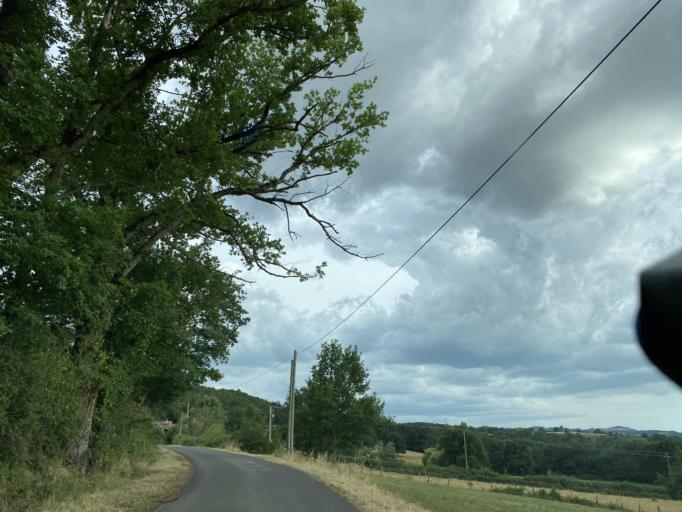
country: FR
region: Auvergne
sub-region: Departement du Puy-de-Dome
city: Peschadoires
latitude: 45.7612
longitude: 3.4512
